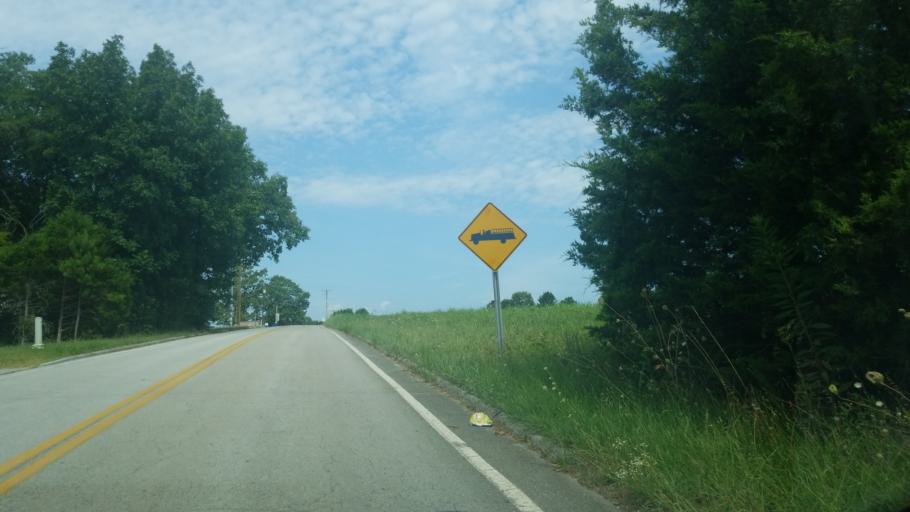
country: US
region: Tennessee
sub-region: Hamilton County
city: Lakesite
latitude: 35.1829
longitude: -85.0600
